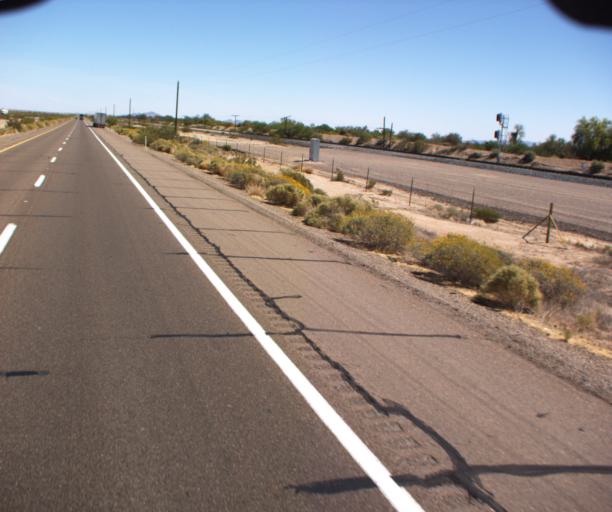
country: US
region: Arizona
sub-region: Yuma County
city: Wellton
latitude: 32.7367
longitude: -113.6979
